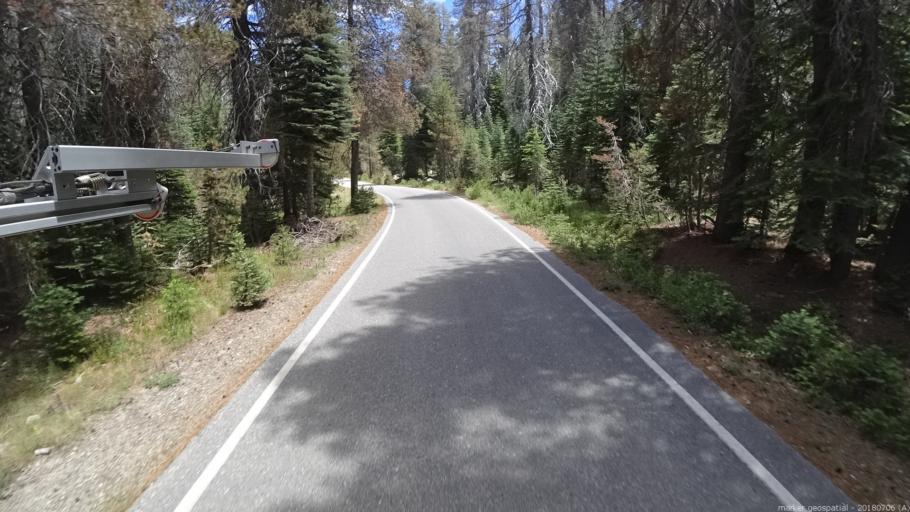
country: US
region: California
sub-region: Madera County
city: Oakhurst
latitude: 37.4445
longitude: -119.4666
